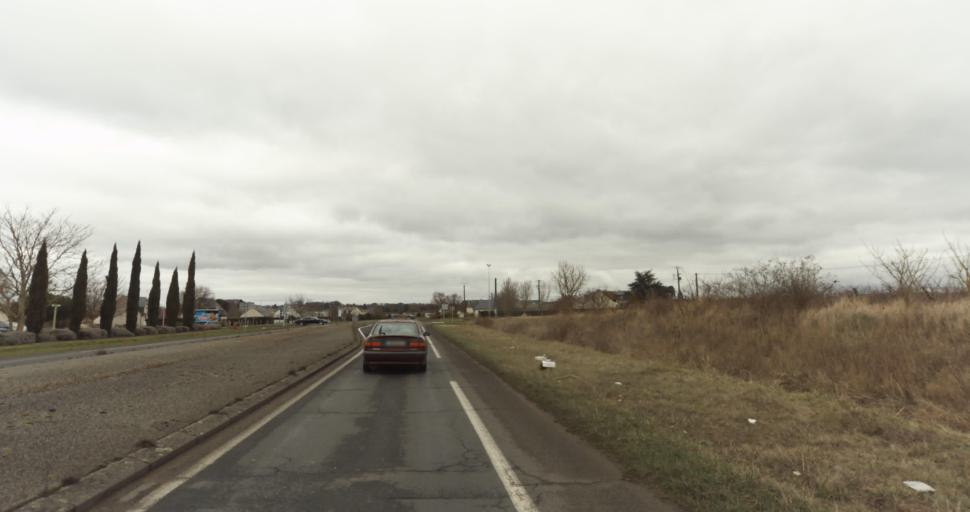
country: FR
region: Pays de la Loire
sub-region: Departement de Maine-et-Loire
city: Varrains
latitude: 47.2163
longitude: -0.0595
